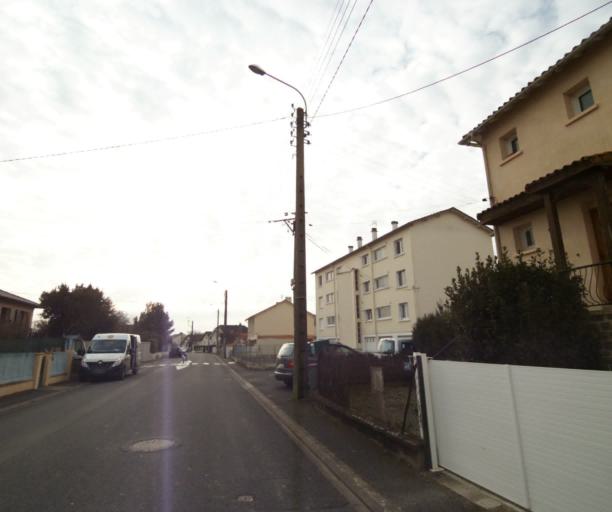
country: FR
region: Poitou-Charentes
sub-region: Departement des Deux-Sevres
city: Niort
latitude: 46.3084
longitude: -0.4566
